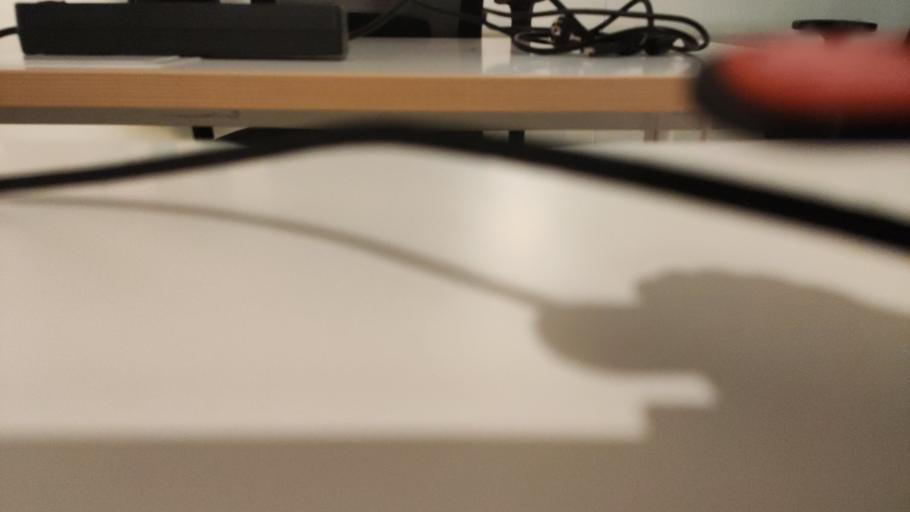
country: RU
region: Moskovskaya
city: Proletarskiy
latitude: 54.9753
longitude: 37.3609
